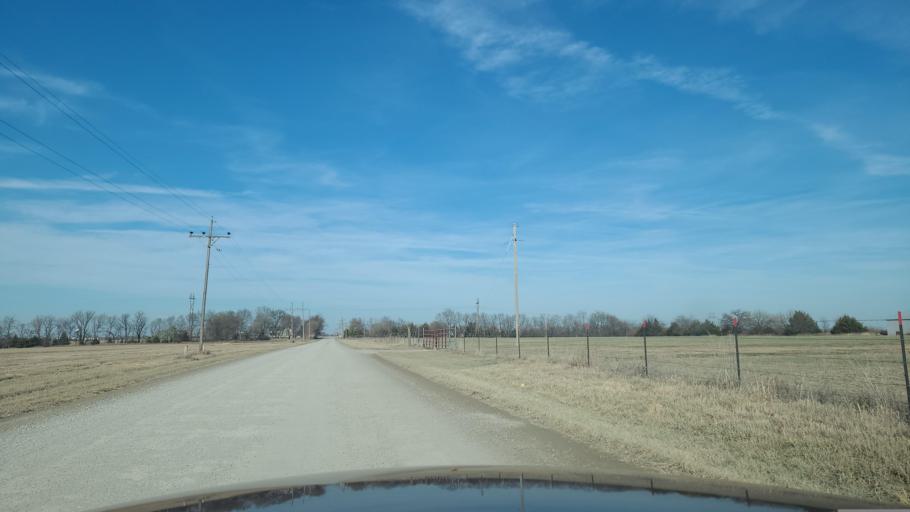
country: US
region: Kansas
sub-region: Douglas County
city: Eudora
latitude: 38.9174
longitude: -95.0748
